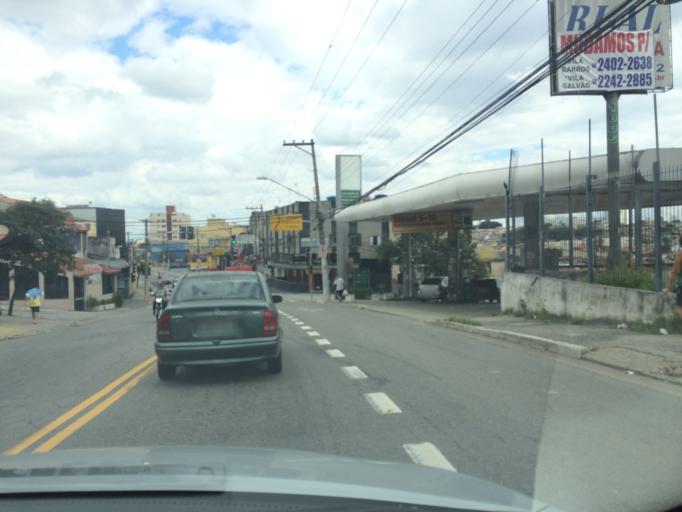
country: BR
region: Sao Paulo
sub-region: Guarulhos
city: Guarulhos
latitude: -23.4464
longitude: -46.5212
